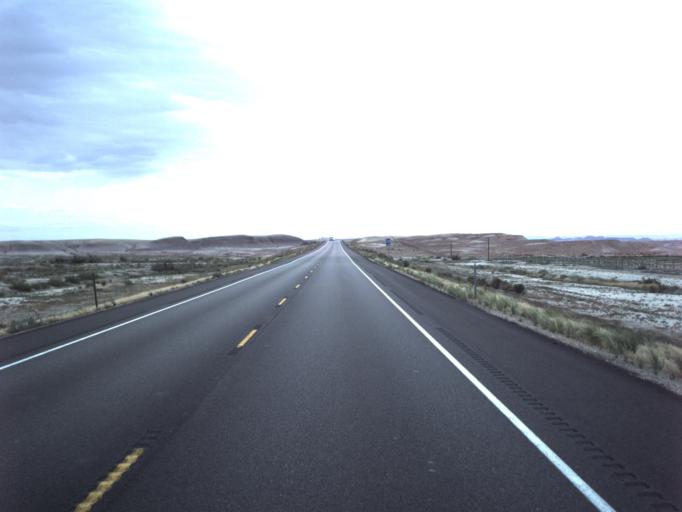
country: US
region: Utah
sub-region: Carbon County
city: East Carbon City
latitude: 38.9943
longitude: -110.2558
